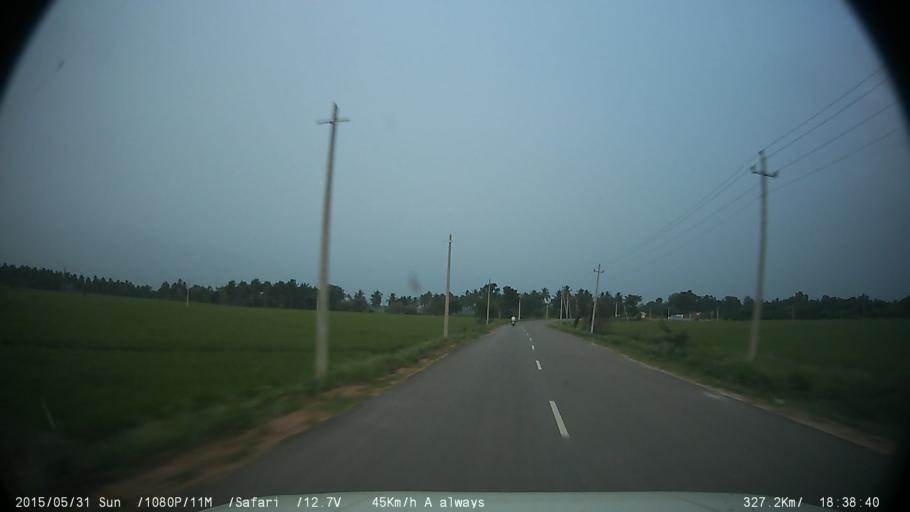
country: IN
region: Karnataka
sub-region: Mysore
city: Nanjangud
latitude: 12.1456
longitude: 76.7789
